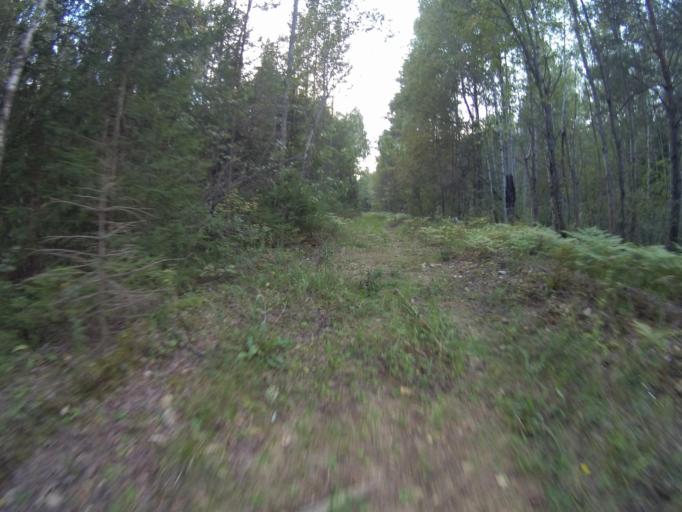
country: RU
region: Vladimir
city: Raduzhnyy
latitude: 55.9824
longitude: 40.2671
